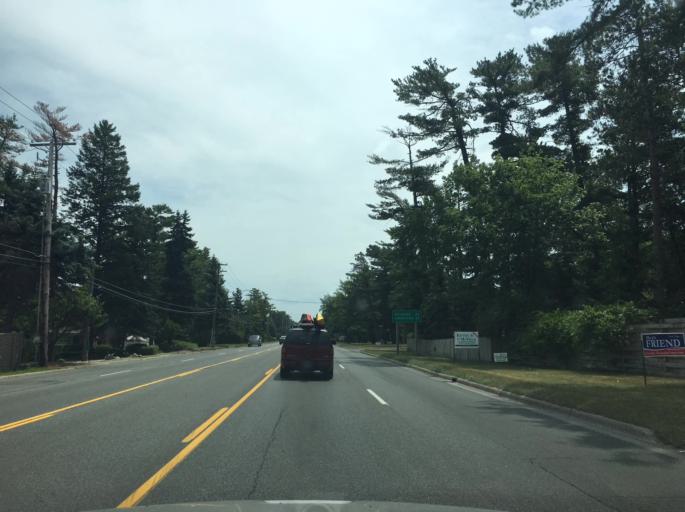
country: US
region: Michigan
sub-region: Grand Traverse County
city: Traverse City
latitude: 44.7544
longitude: -85.5716
